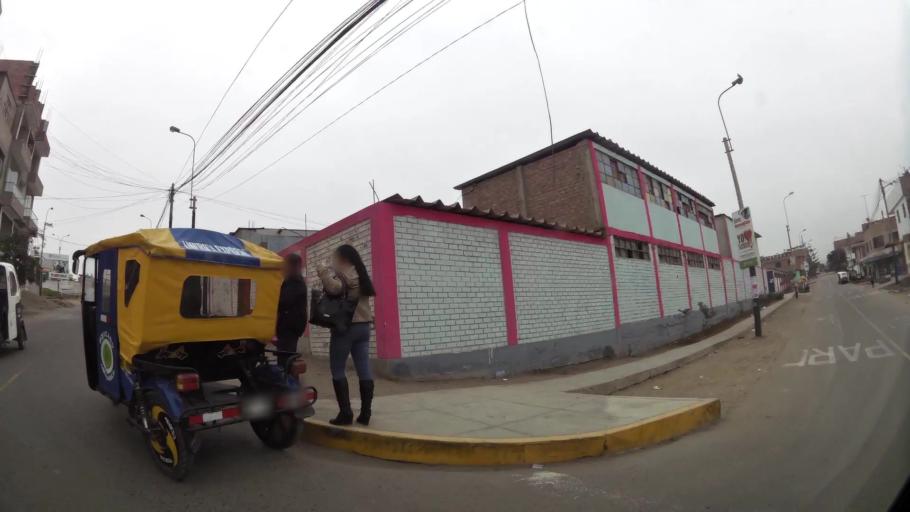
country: PE
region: Lima
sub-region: Lima
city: Surco
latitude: -12.1980
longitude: -76.9747
